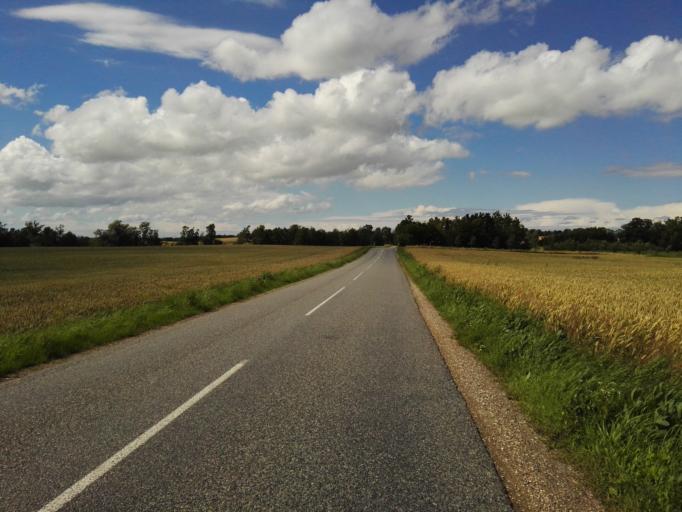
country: DK
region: Capital Region
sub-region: Egedal Kommune
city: Ganlose
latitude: 55.7900
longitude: 12.2329
